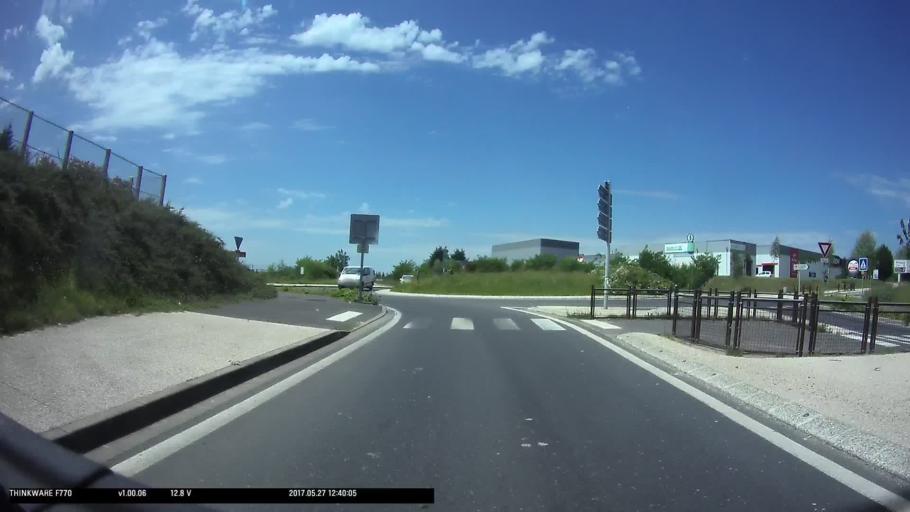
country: FR
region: Haute-Normandie
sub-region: Departement de l'Eure
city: Gisors
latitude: 49.2751
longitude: 1.7638
